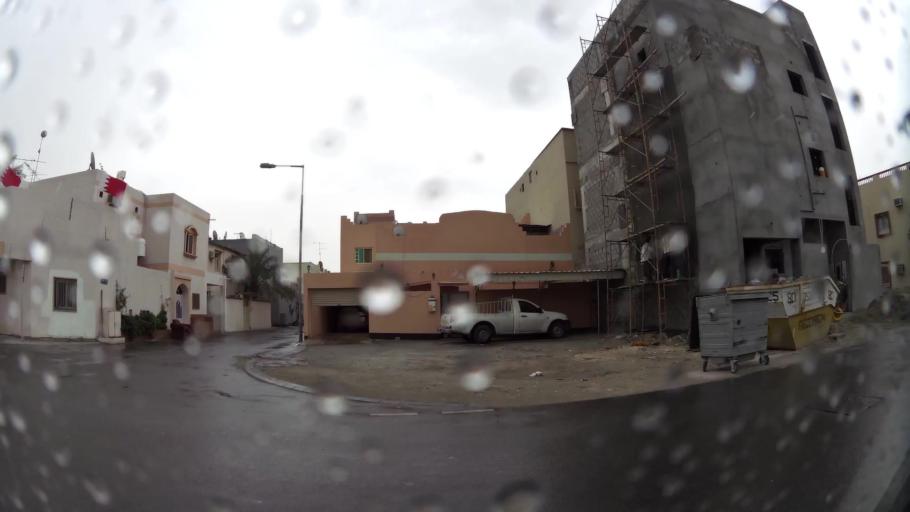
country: BH
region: Northern
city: Madinat `Isa
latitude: 26.1736
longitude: 50.5571
